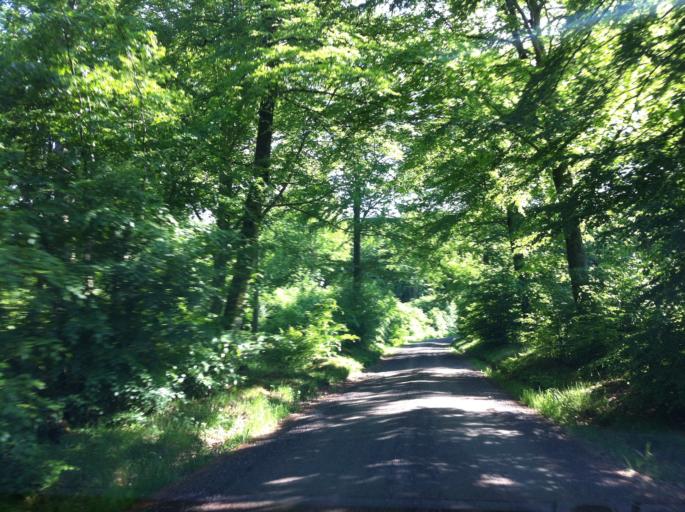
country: SE
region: Skane
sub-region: Klippans Kommun
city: Ljungbyhed
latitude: 56.0536
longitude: 13.2206
